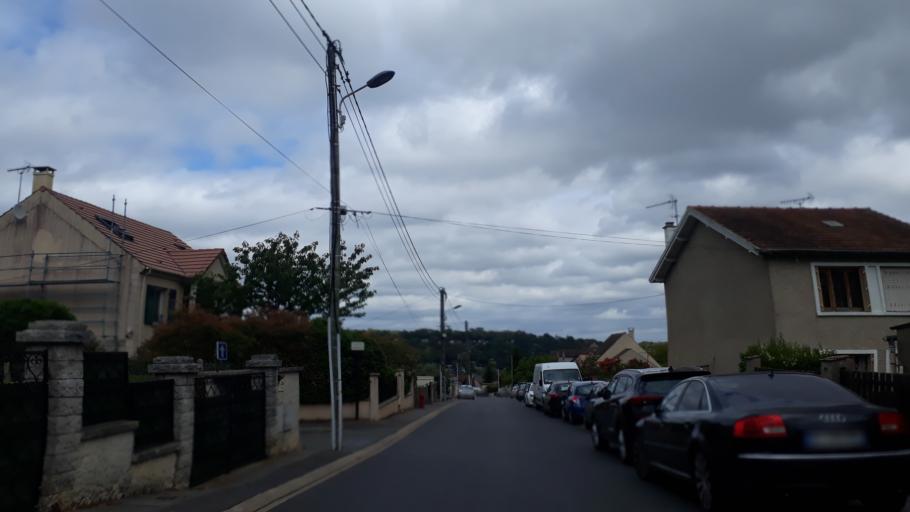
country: FR
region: Ile-de-France
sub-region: Departement de l'Essonne
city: Nozay
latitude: 48.6654
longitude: 2.2523
